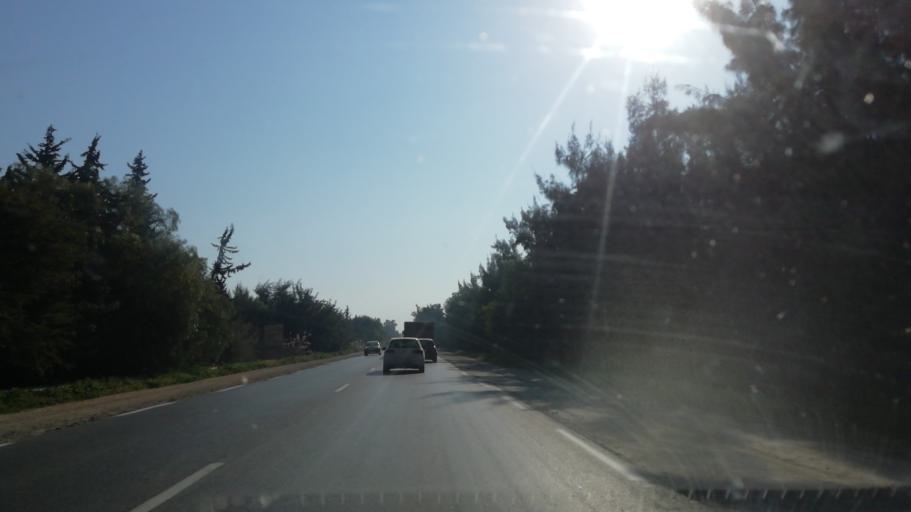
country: DZ
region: Relizane
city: Relizane
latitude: 35.7302
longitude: 0.4737
